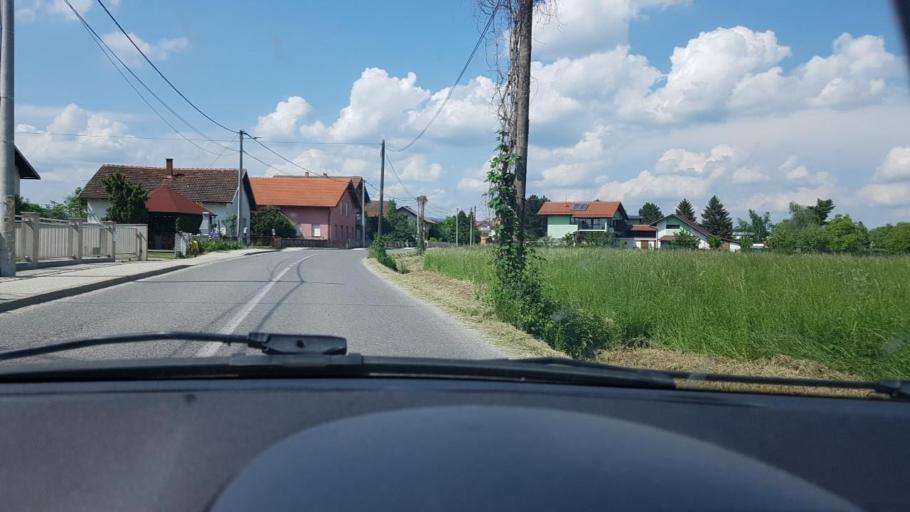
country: HR
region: Grad Zagreb
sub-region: Sesvete
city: Sesvete
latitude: 45.8824
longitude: 16.1735
